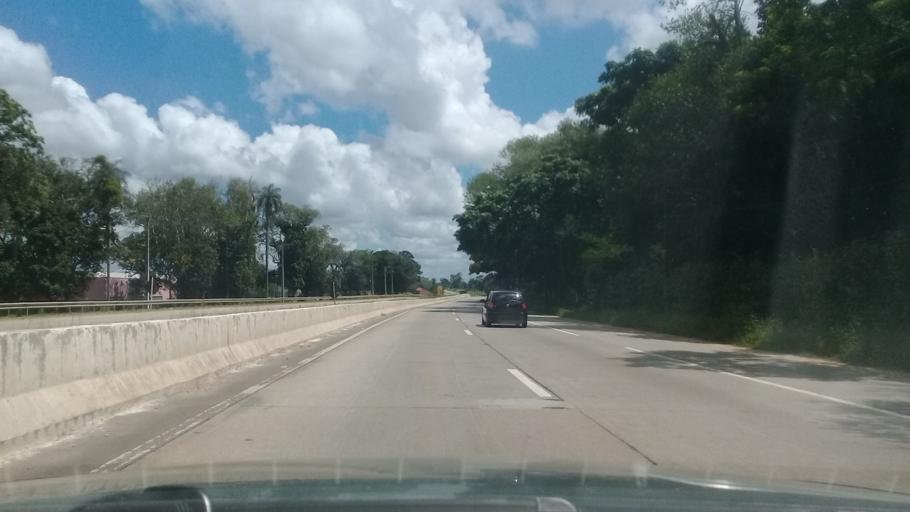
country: BR
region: Pernambuco
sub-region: Carpina
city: Carpina
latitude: -7.9233
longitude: -35.1557
